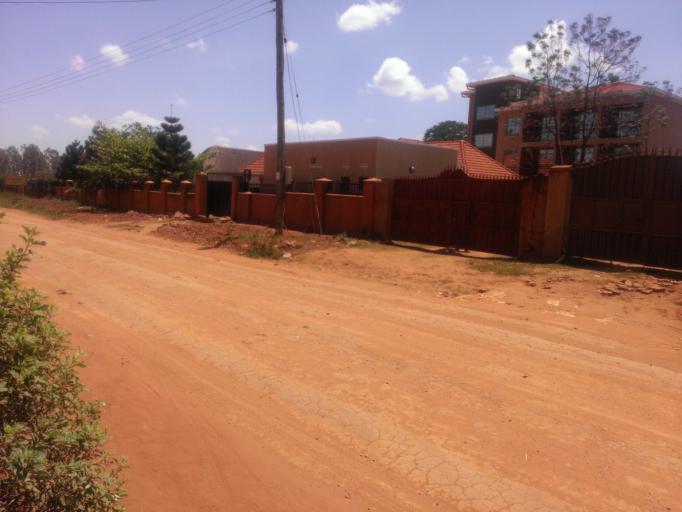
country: UG
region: Northern Region
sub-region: Gulu District
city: Gulu
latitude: 2.7857
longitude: 32.3025
